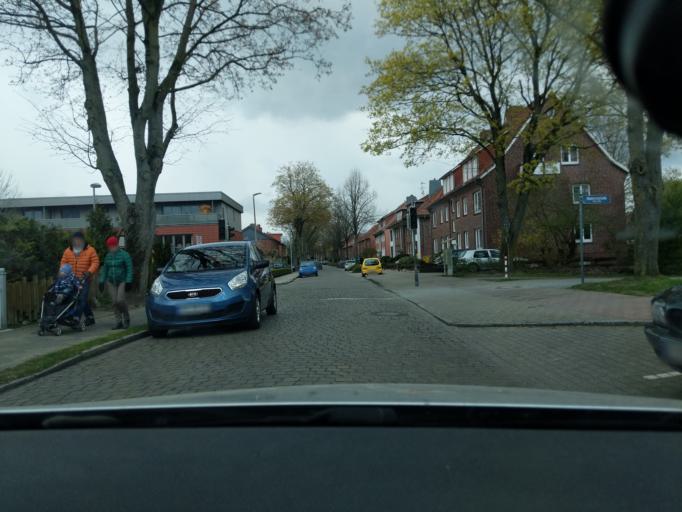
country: DE
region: Lower Saxony
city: Stade
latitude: 53.5888
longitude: 9.4629
